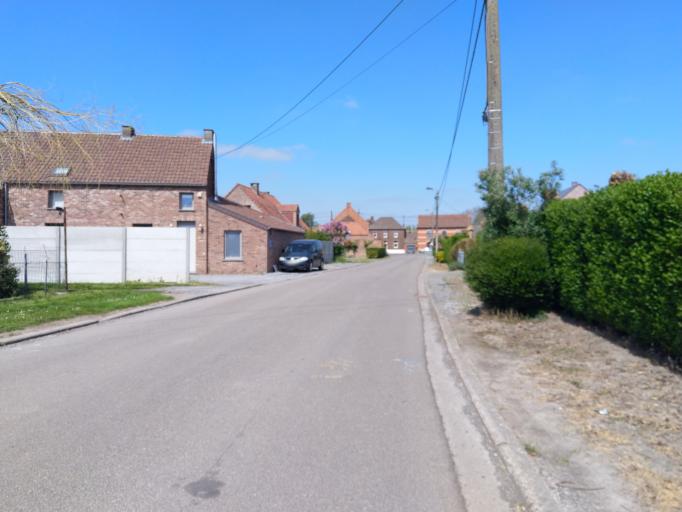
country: BE
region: Wallonia
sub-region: Province du Hainaut
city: Lens
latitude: 50.5272
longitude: 3.8531
